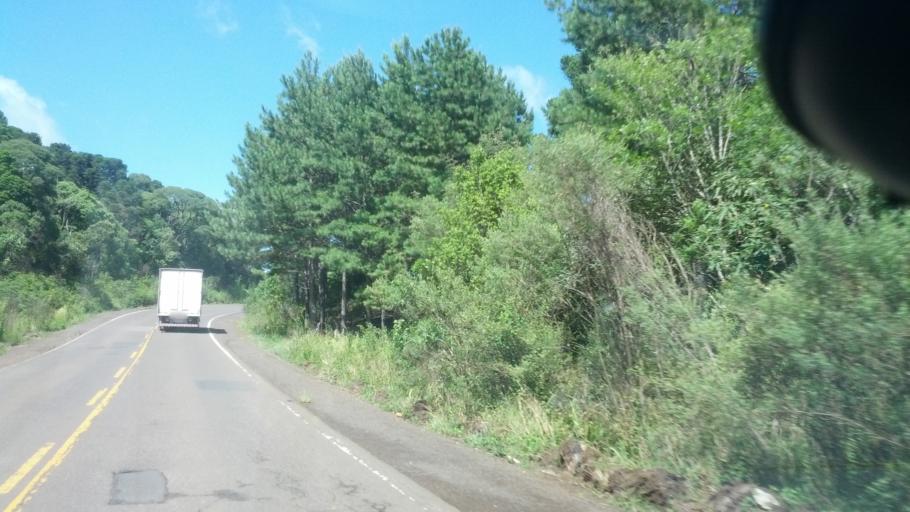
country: BR
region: Santa Catarina
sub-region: Lages
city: Lages
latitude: -27.9259
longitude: -50.5476
